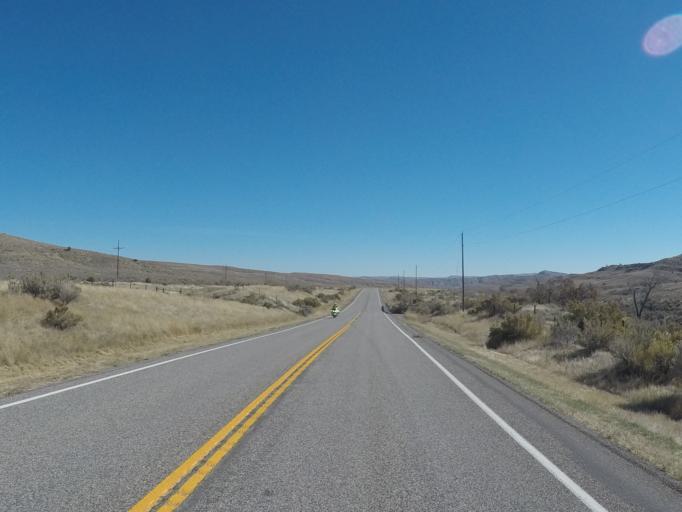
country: US
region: Montana
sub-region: Carbon County
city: Red Lodge
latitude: 45.1546
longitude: -109.0705
